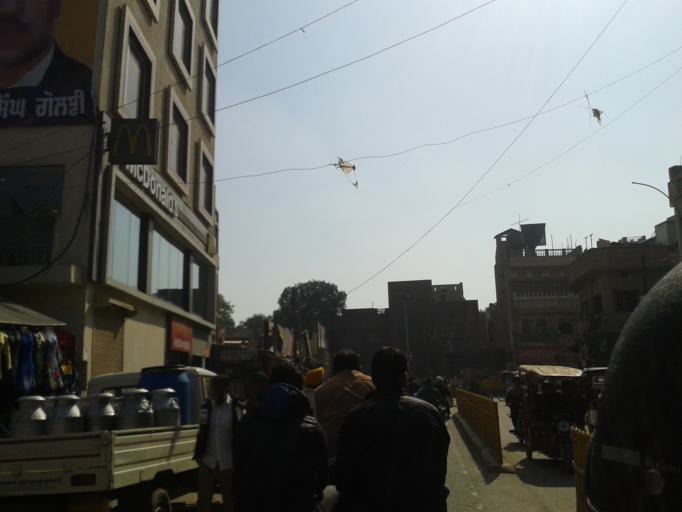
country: IN
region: Punjab
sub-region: Amritsar
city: Amritsar
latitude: 31.6222
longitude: 74.8796
